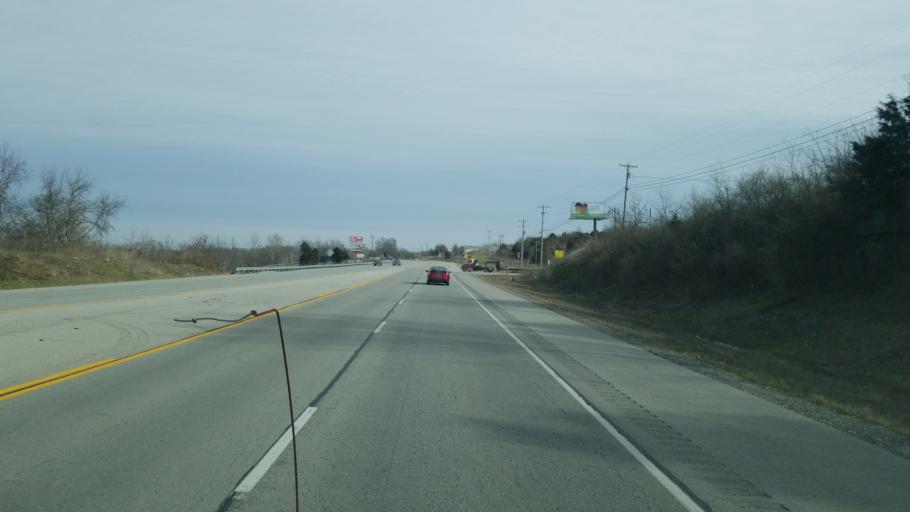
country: US
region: Kentucky
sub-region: Jessamine County
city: Wilmore
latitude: 37.7479
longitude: -84.6235
